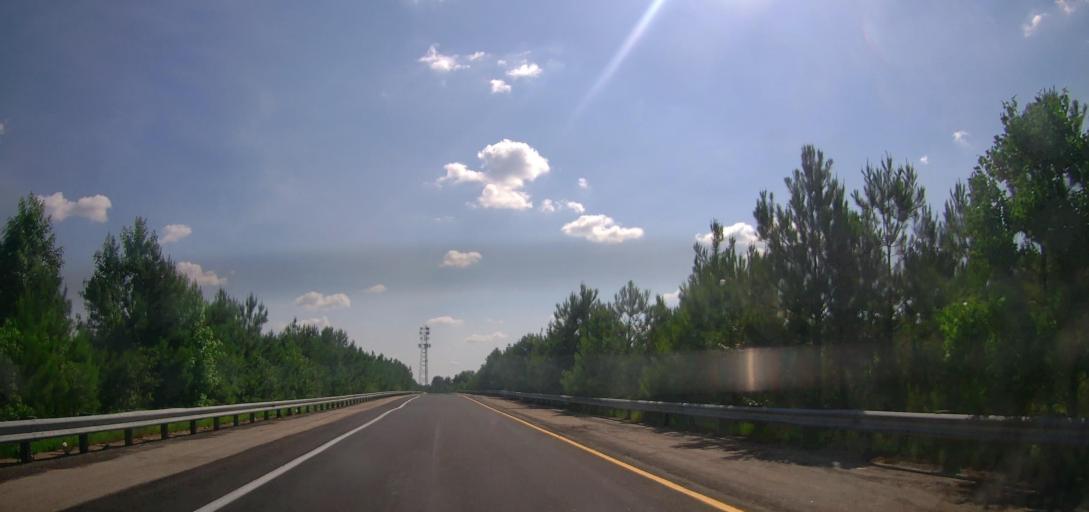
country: US
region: Georgia
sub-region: Henry County
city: Hampton
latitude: 33.3773
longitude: -84.2916
